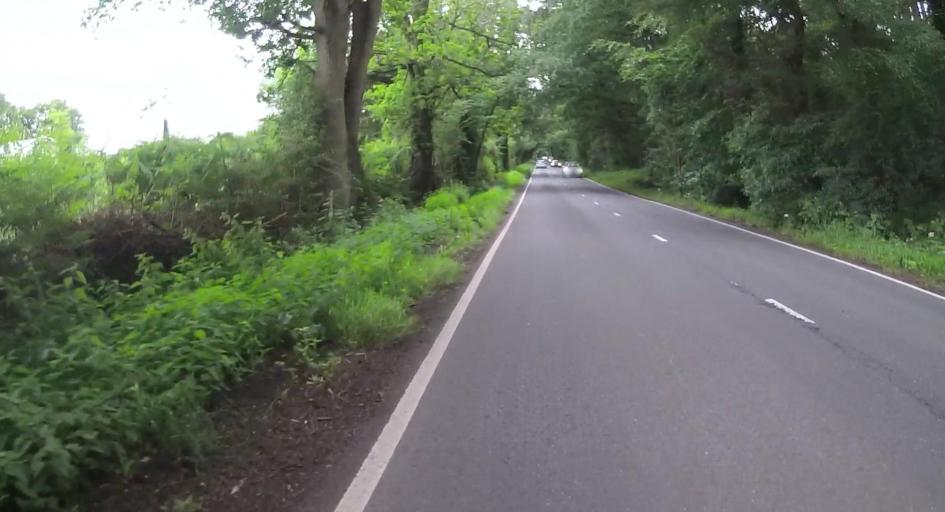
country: GB
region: England
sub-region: Bracknell Forest
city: Crowthorne
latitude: 51.3879
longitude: -0.8162
